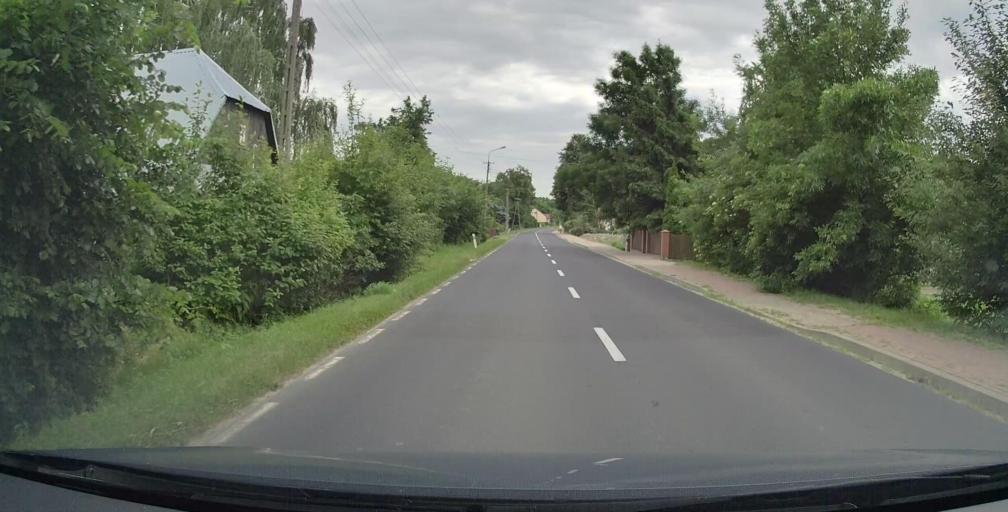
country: PL
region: Masovian Voivodeship
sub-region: Powiat losicki
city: Sarnaki
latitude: 52.3065
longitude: 22.9541
